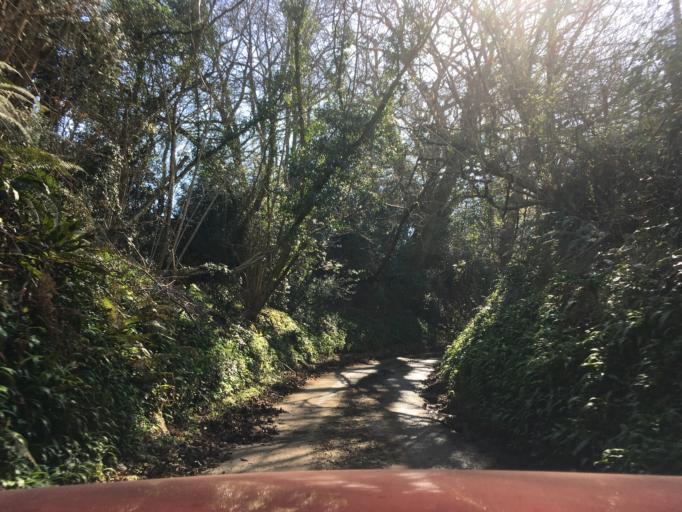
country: GB
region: England
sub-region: Gloucestershire
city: Dursley
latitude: 51.6600
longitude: -2.3482
